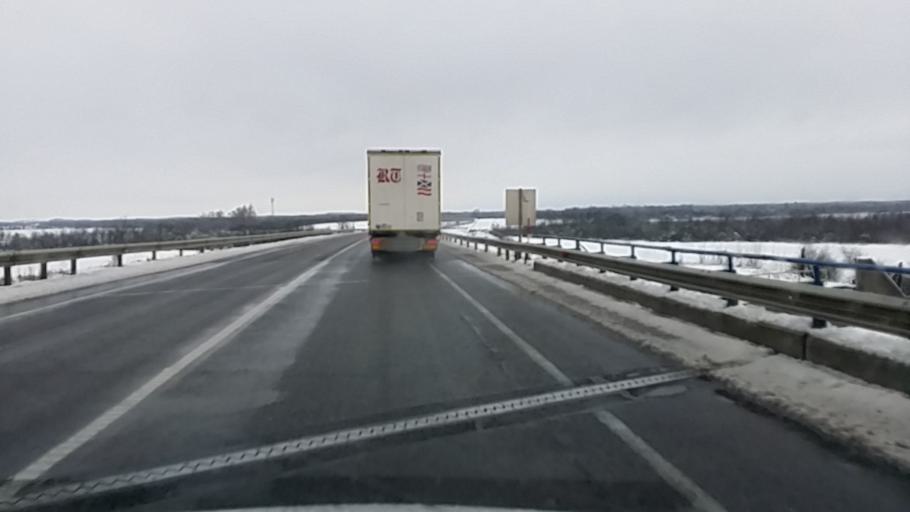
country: HU
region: Gyor-Moson-Sopron
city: Rajka
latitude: 47.9357
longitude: 17.1681
